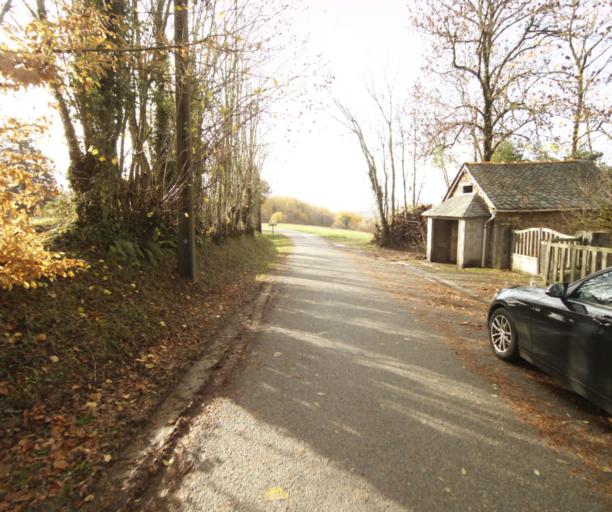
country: FR
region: Limousin
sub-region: Departement de la Correze
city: Sainte-Fereole
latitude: 45.2253
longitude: 1.6260
